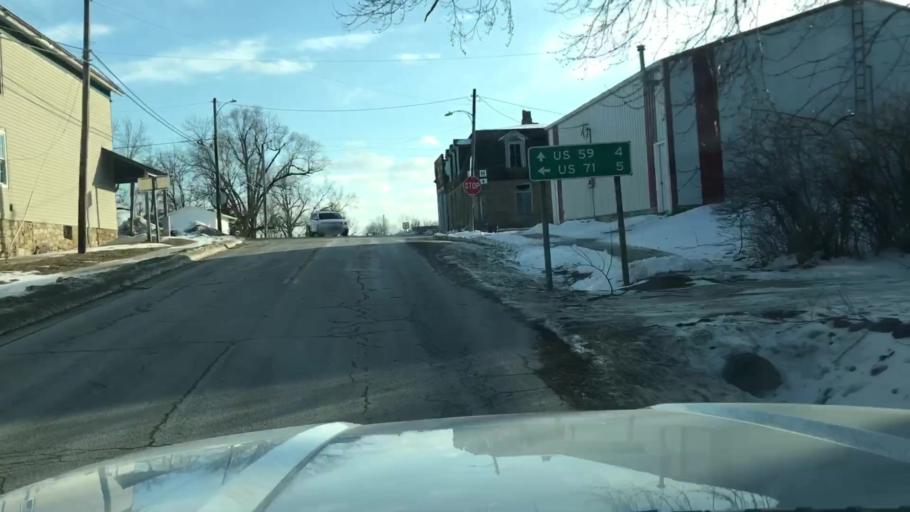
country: US
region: Missouri
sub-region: Andrew County
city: Savannah
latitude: 40.0256
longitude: -94.9738
